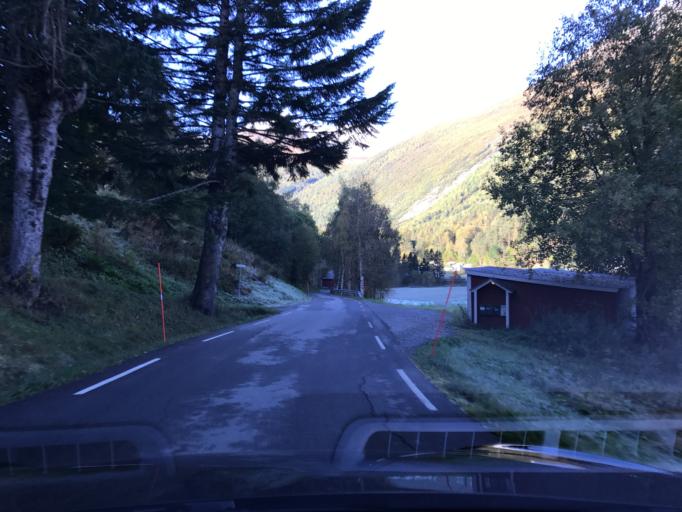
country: NO
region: More og Romsdal
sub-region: Norddal
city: Valldal
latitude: 62.3144
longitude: 7.2974
